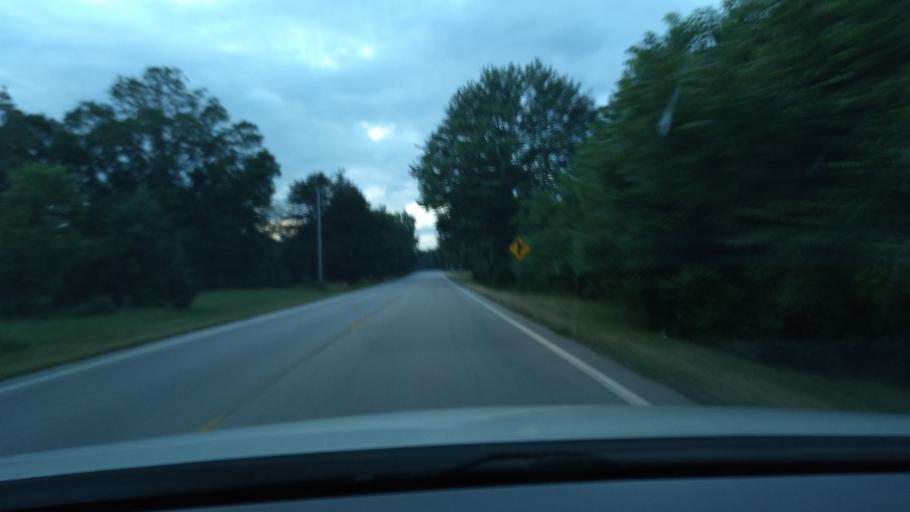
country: US
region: North Carolina
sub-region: Rockingham County
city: Reidsville
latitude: 36.3927
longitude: -79.5589
